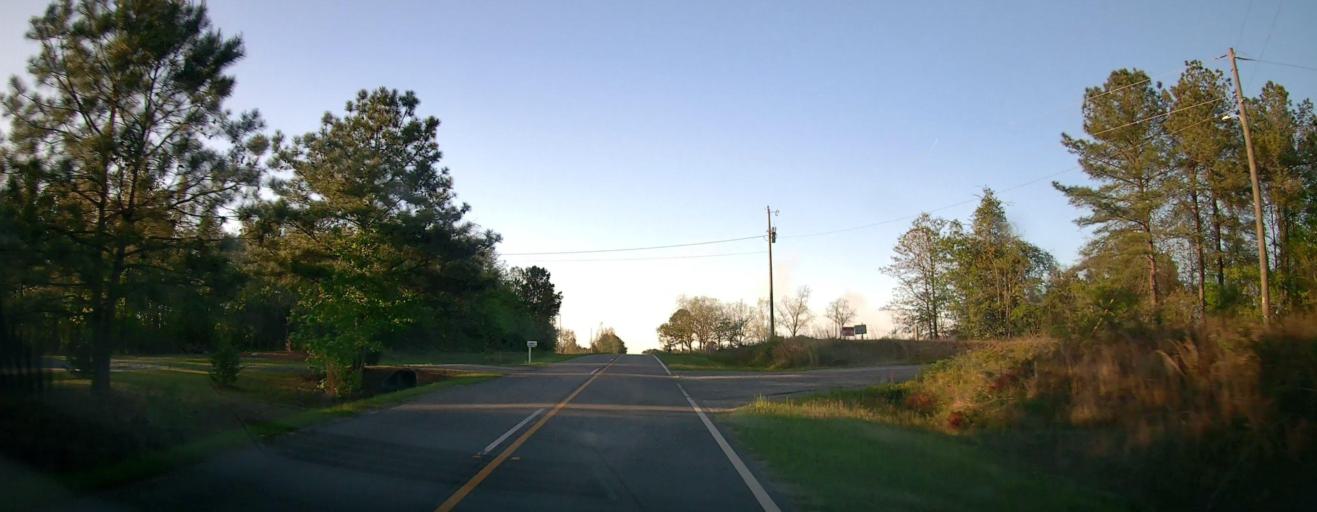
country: US
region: Georgia
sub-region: Marion County
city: Buena Vista
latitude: 32.4520
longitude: -84.4253
